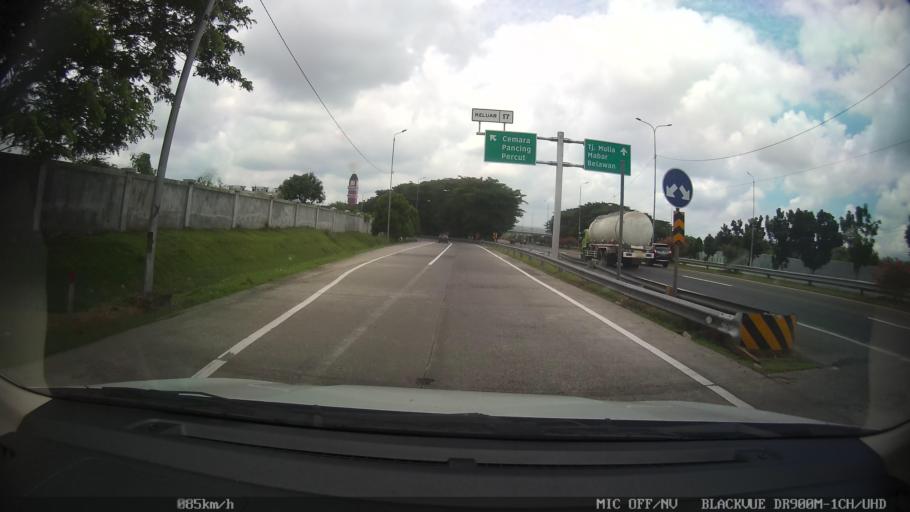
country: ID
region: North Sumatra
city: Medan
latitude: 3.6350
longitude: 98.7106
